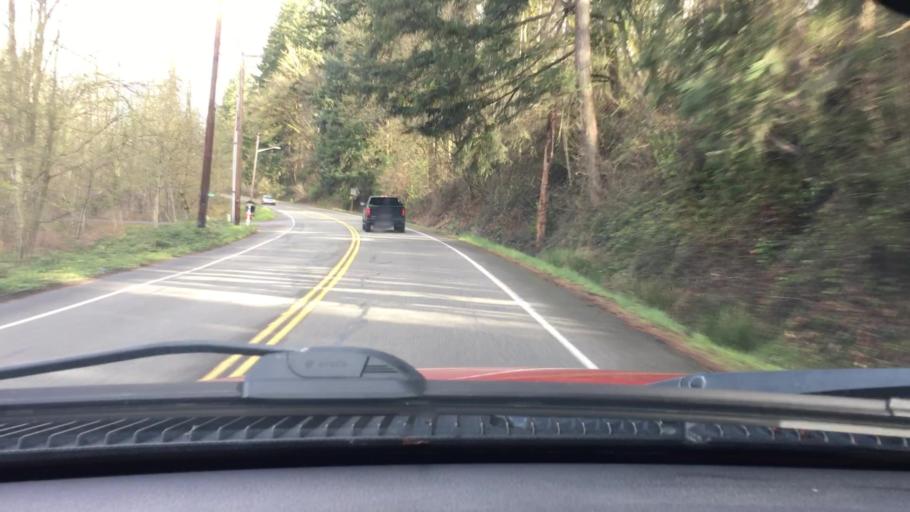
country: US
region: Washington
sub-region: King County
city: Maple Valley
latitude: 47.3690
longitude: -122.0441
